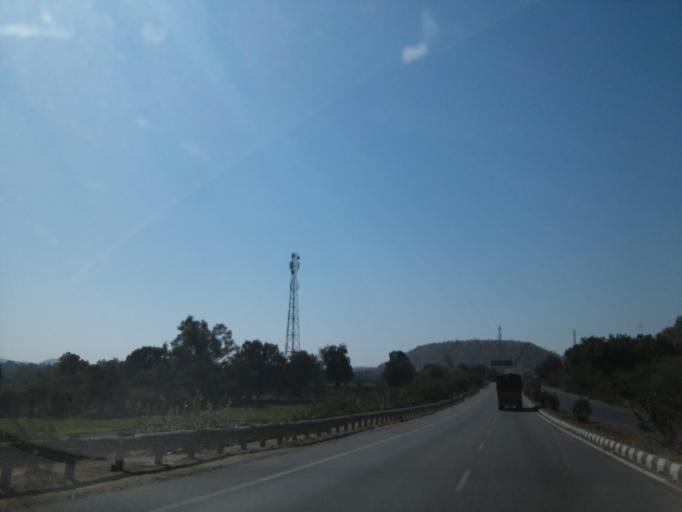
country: IN
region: Rajasthan
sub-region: Dungarpur
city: Dungarpur
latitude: 24.0082
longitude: 73.6565
